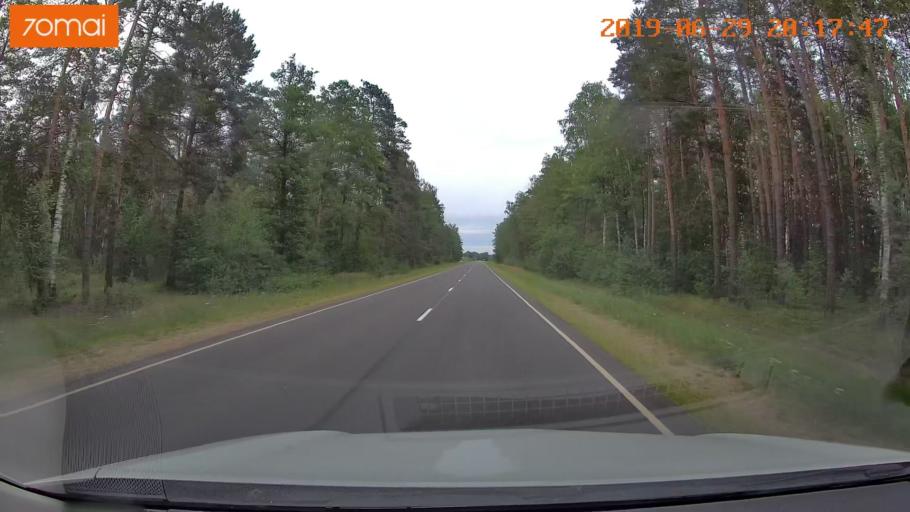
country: BY
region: Brest
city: Asnyezhytsy
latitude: 52.3904
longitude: 26.2232
